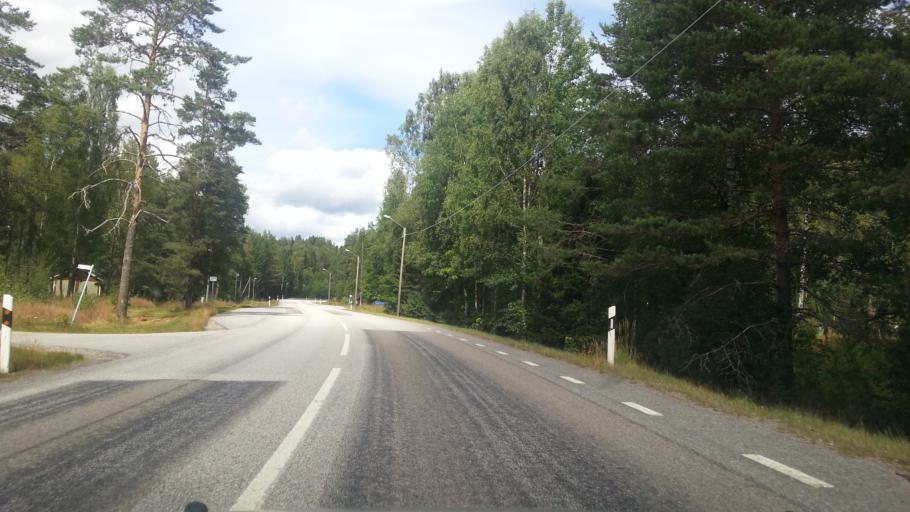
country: SE
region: Vaestmanland
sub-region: Skinnskattebergs Kommun
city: Skinnskatteberg
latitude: 59.8210
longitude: 15.5331
